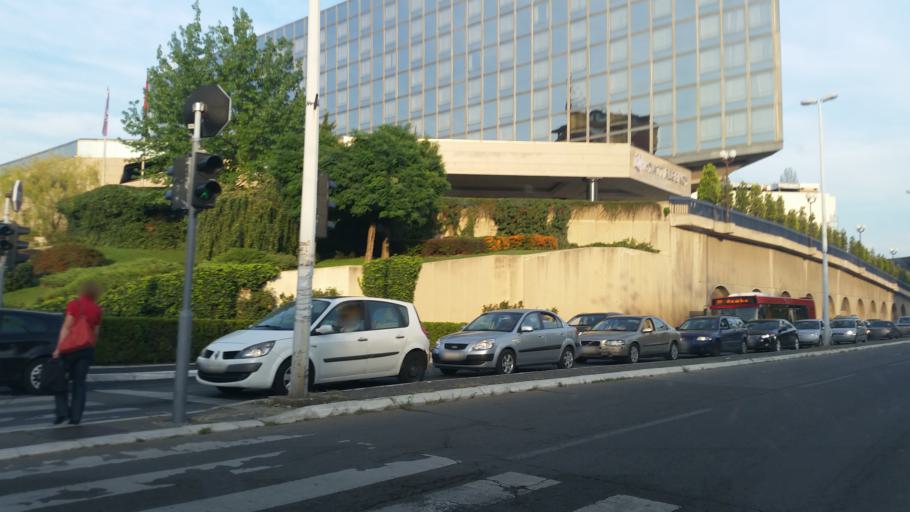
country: RS
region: Central Serbia
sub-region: Belgrade
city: Novi Beograd
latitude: 44.8129
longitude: 20.4332
